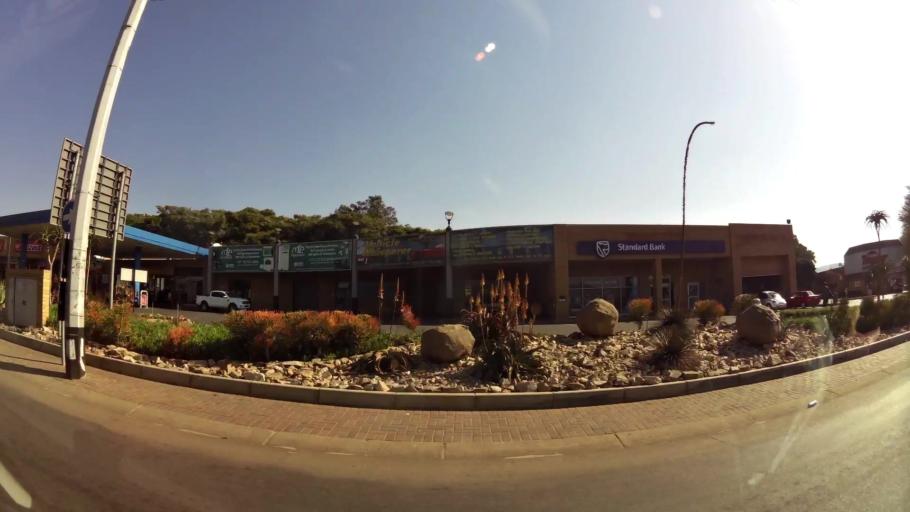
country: ZA
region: Gauteng
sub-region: City of Tshwane Metropolitan Municipality
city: Pretoria
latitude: -25.7189
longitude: 28.2026
